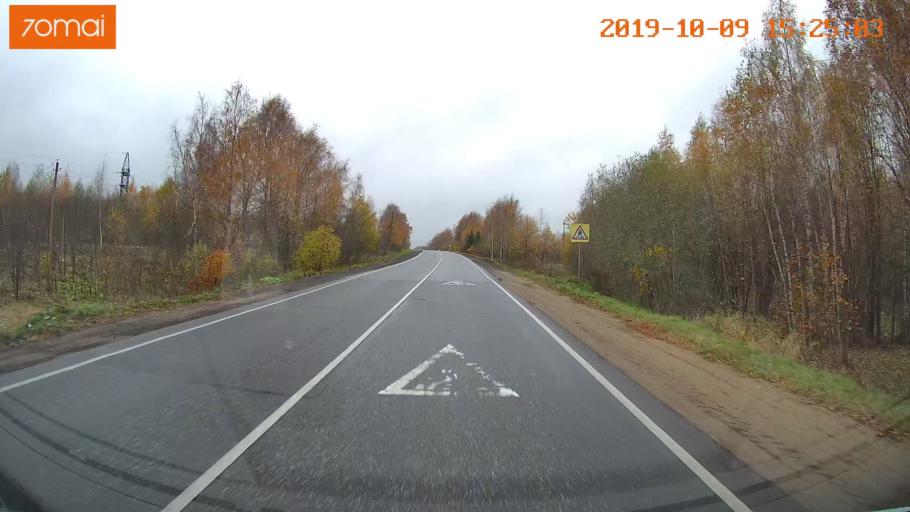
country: RU
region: Kostroma
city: Susanino
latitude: 58.0295
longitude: 41.4378
